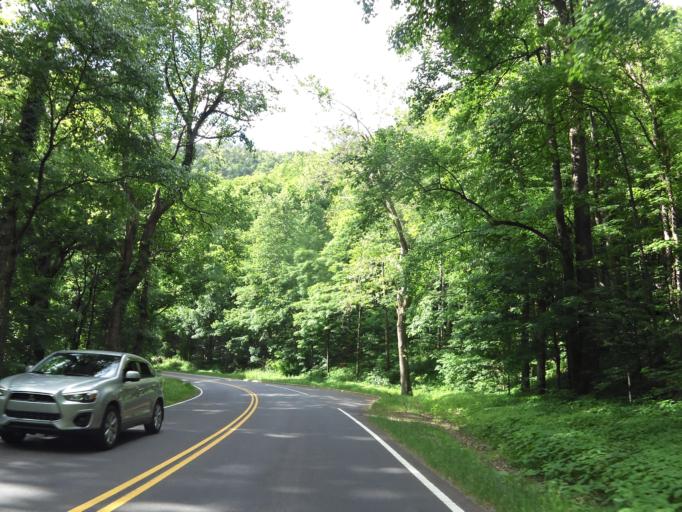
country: US
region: Tennessee
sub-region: Sevier County
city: Gatlinburg
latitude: 35.6400
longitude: -83.4948
